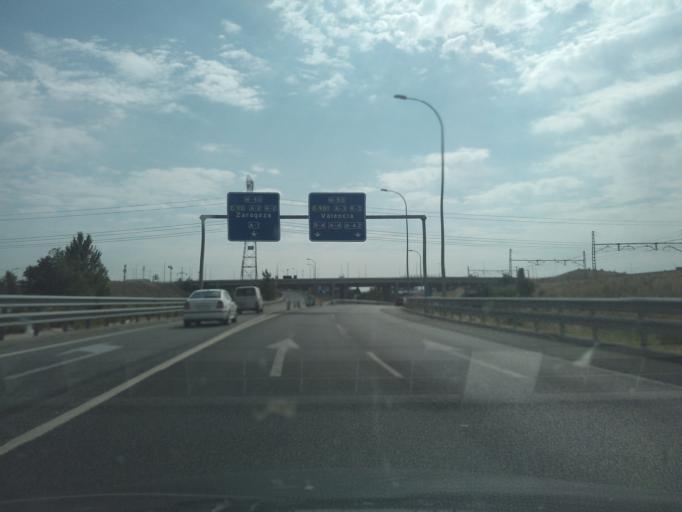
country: ES
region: Madrid
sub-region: Provincia de Madrid
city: San Fernando de Henares
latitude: 40.4460
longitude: -3.5219
